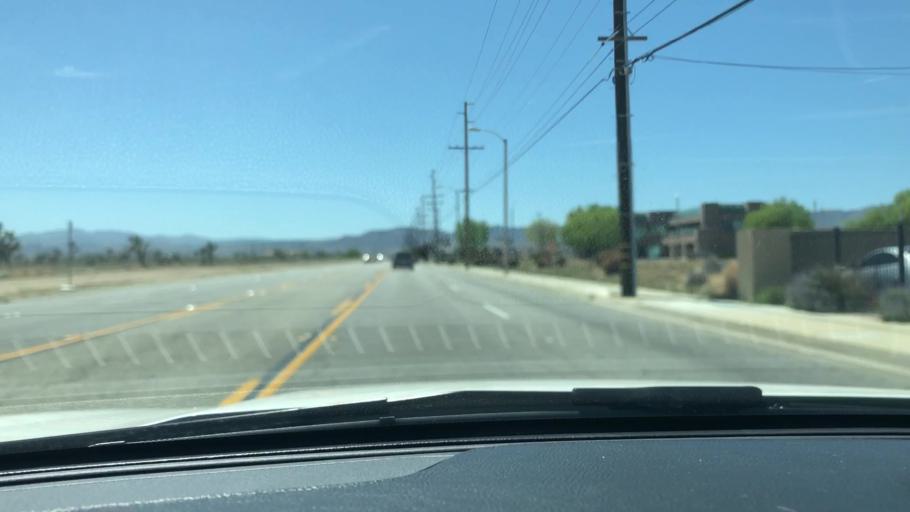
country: US
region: California
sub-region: Los Angeles County
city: Desert View Highlands
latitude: 34.6433
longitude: -118.1478
